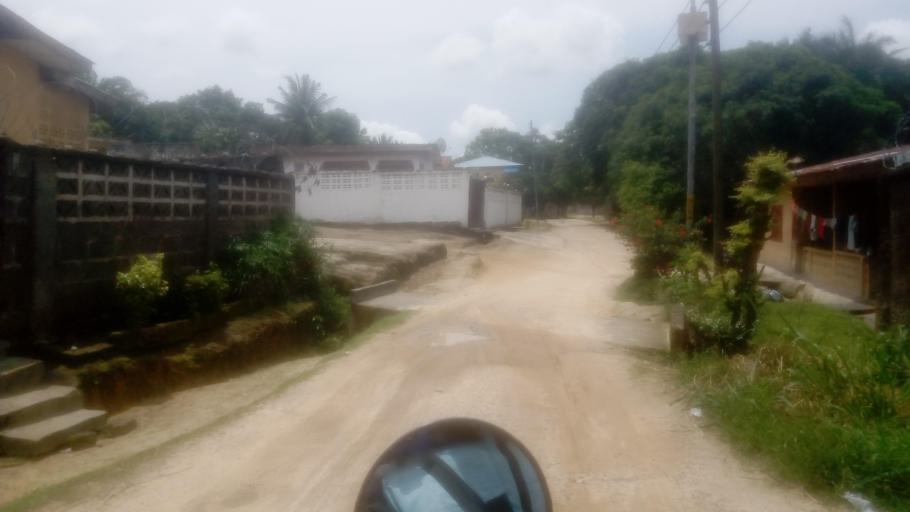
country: SL
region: Southern Province
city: Bo
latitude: 7.9509
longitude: -11.7133
